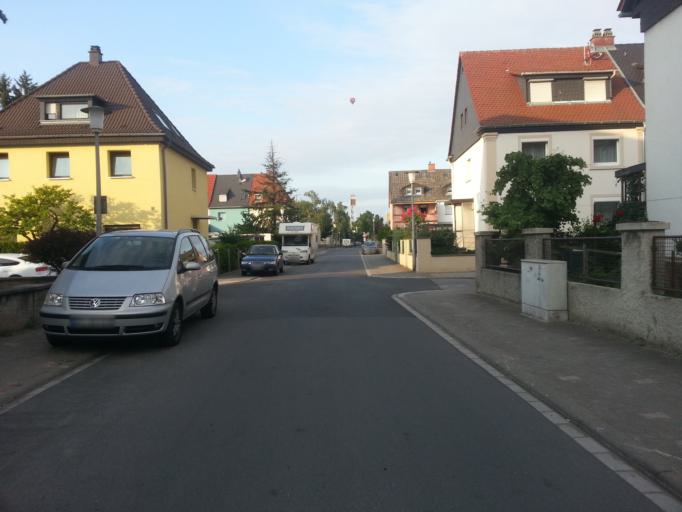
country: DE
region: Baden-Wuerttemberg
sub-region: Karlsruhe Region
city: Mannheim
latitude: 49.5033
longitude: 8.5075
